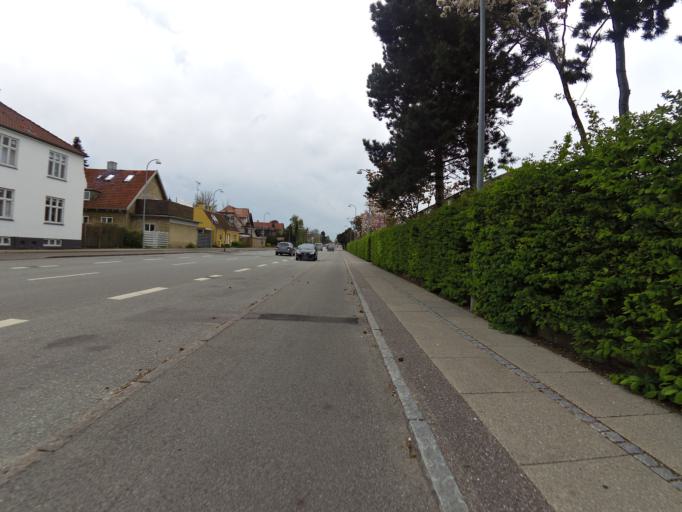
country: DK
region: Capital Region
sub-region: Gladsaxe Municipality
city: Buddinge
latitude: 55.7419
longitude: 12.5104
